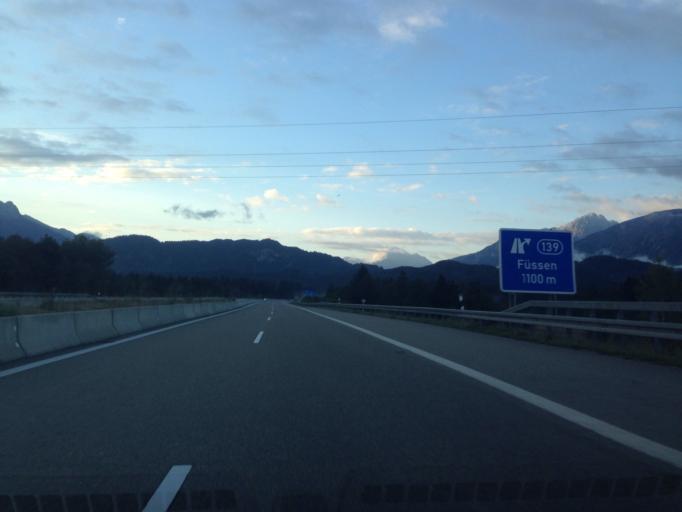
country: DE
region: Bavaria
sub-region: Swabia
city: Hopferau
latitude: 47.5893
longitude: 10.6578
